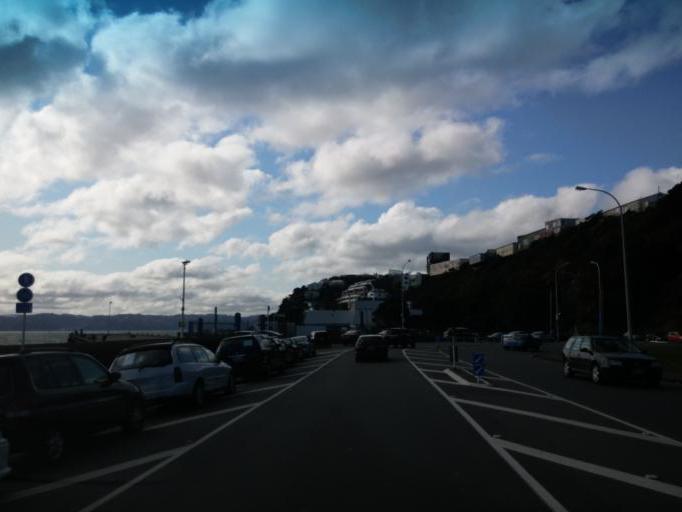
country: NZ
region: Wellington
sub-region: Wellington City
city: Wellington
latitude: -41.3150
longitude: 174.8106
